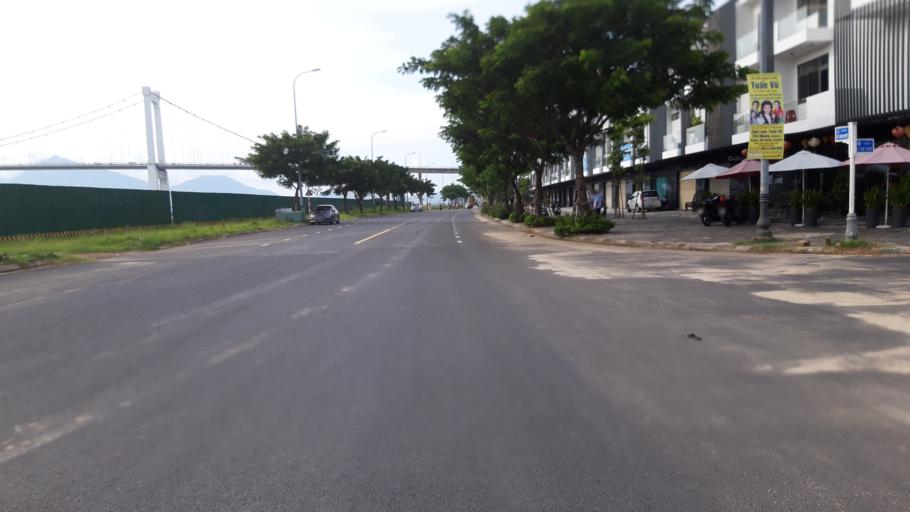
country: VN
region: Da Nang
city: Da Nang
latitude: 16.0927
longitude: 108.2255
